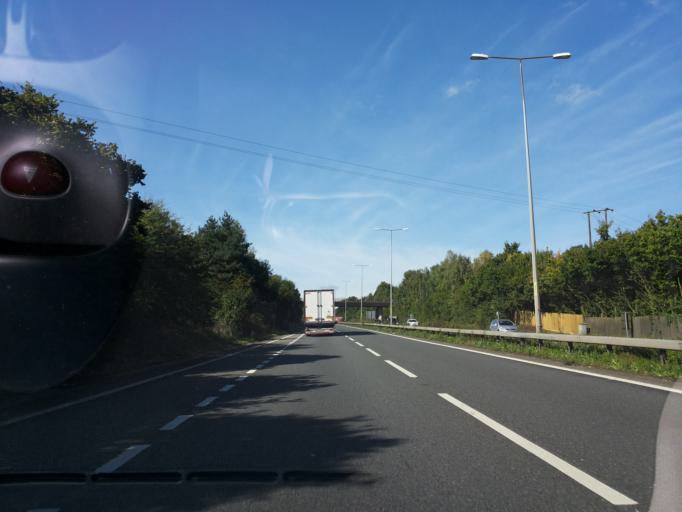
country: GB
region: England
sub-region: Kent
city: Blean
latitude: 51.2840
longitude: 1.0292
